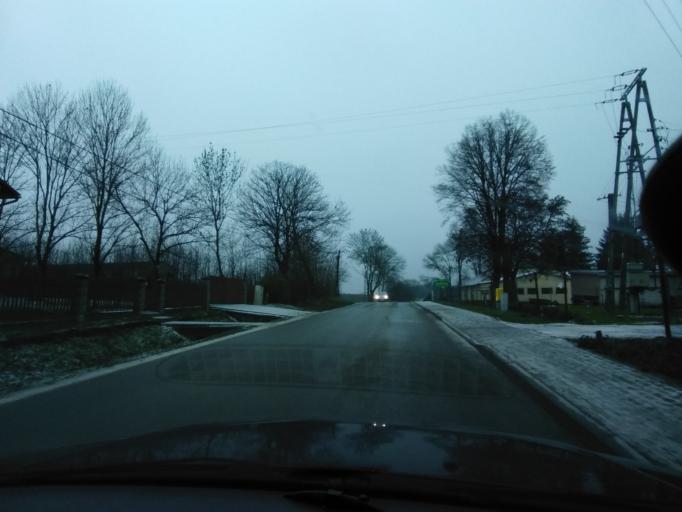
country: PL
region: Subcarpathian Voivodeship
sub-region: Powiat przeworski
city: Urzejowice
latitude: 50.0059
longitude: 22.4361
